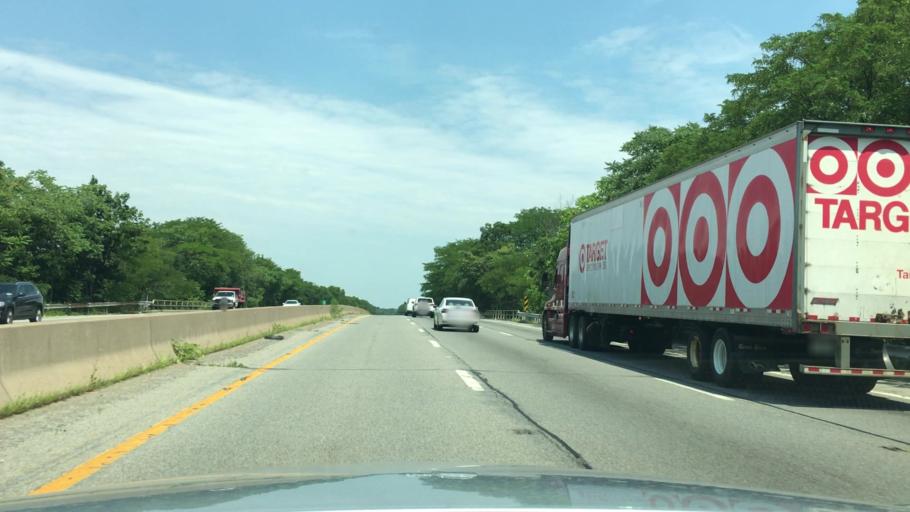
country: US
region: New York
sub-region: Nassau County
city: Bethpage
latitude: 40.7547
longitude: -73.4745
